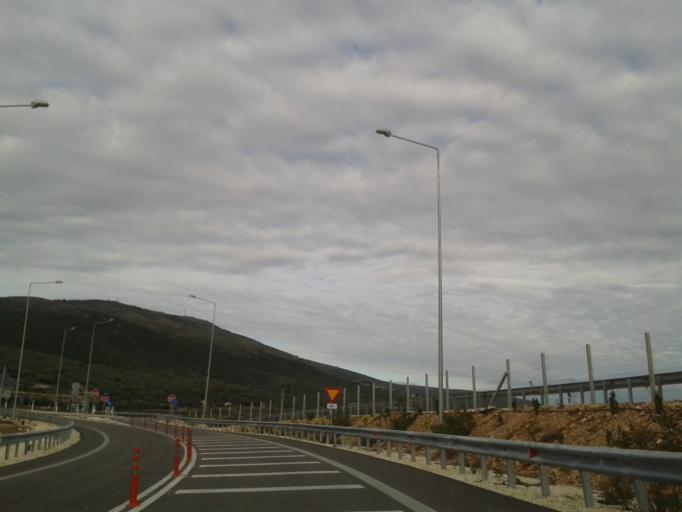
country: GR
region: West Greece
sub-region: Nomos Aitolias kai Akarnanias
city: Stanos
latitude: 38.7777
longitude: 21.1912
